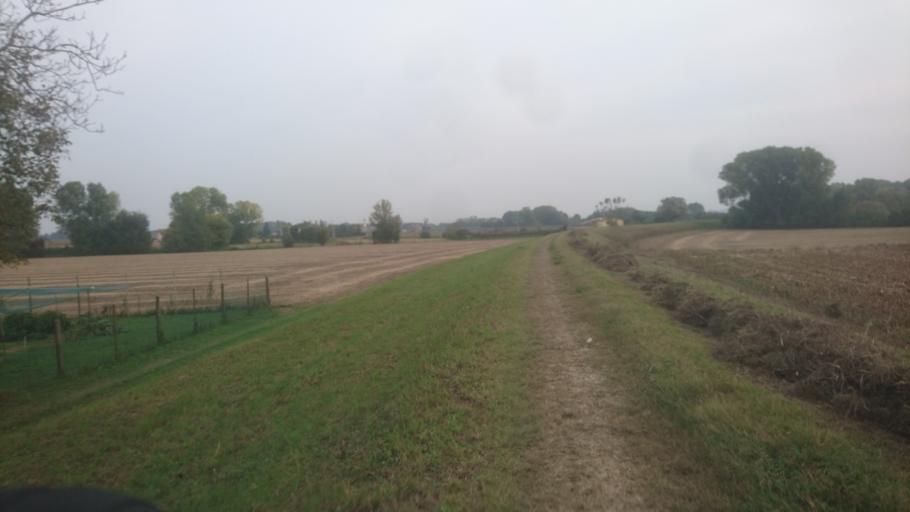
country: IT
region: Veneto
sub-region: Provincia di Padova
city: Cervarese Santa Croce
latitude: 45.4217
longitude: 11.7082
